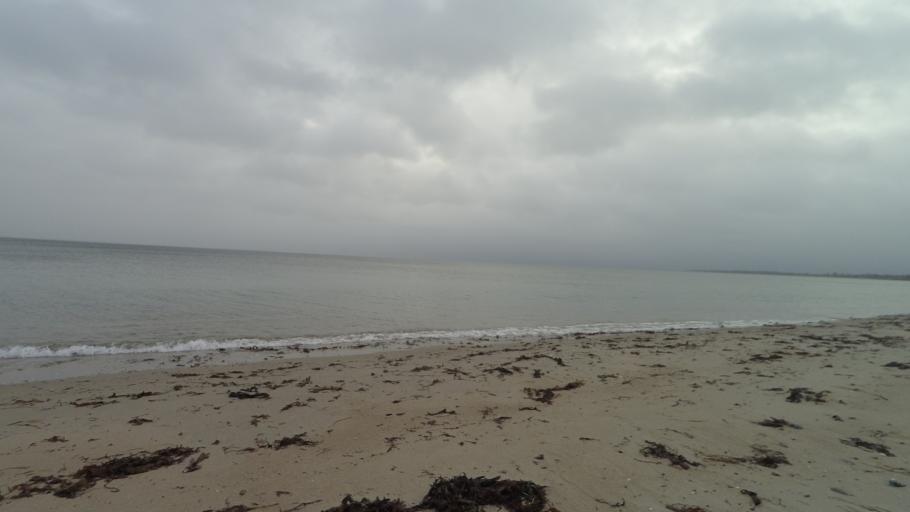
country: DK
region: Central Jutland
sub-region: Arhus Kommune
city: Malling
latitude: 55.9958
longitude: 10.2556
